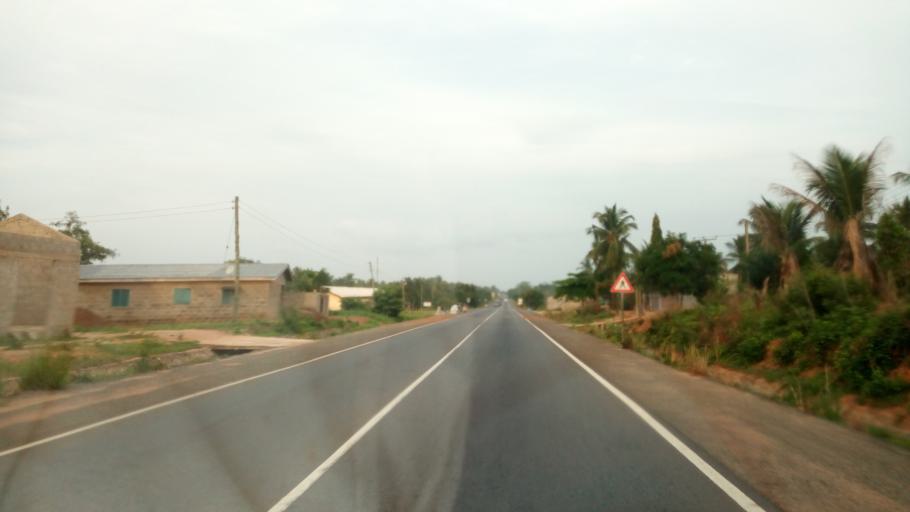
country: TG
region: Maritime
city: Lome
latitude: 6.0958
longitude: 1.0837
